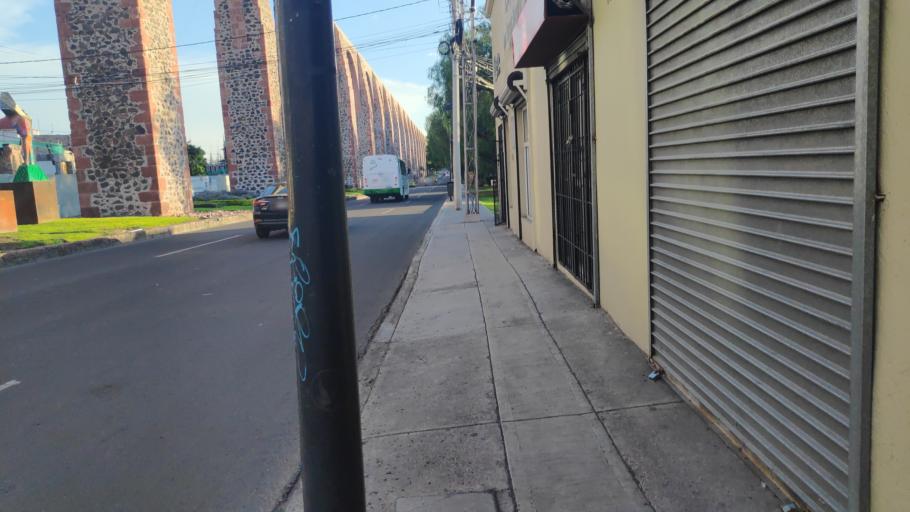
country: MX
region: Queretaro
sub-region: Queretaro
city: Santiago de Queretaro
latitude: 20.5962
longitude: -100.3731
